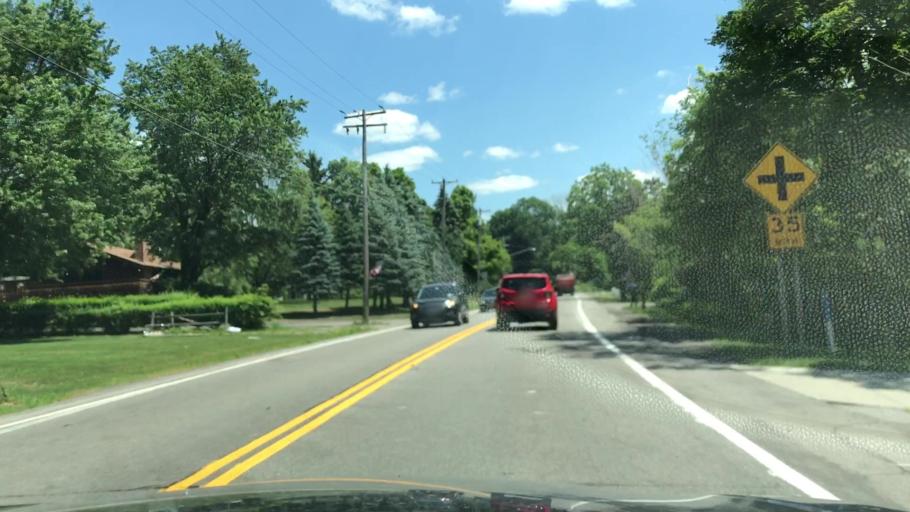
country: US
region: New York
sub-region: Erie County
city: East Aurora
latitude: 42.7676
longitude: -78.5799
